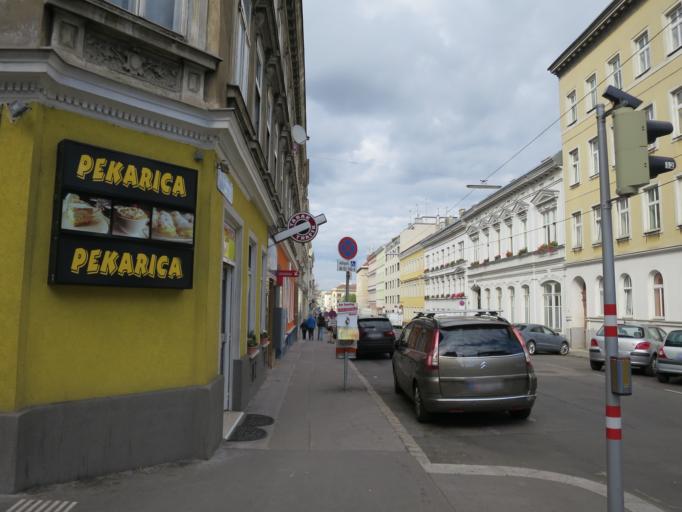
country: AT
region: Vienna
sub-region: Wien Stadt
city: Vienna
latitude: 48.2069
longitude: 16.3321
